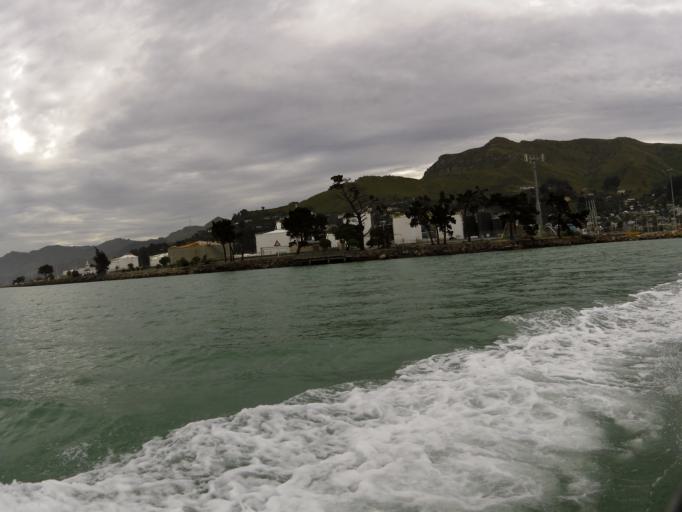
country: NZ
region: Canterbury
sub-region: Christchurch City
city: Christchurch
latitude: -43.6082
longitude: 172.7181
